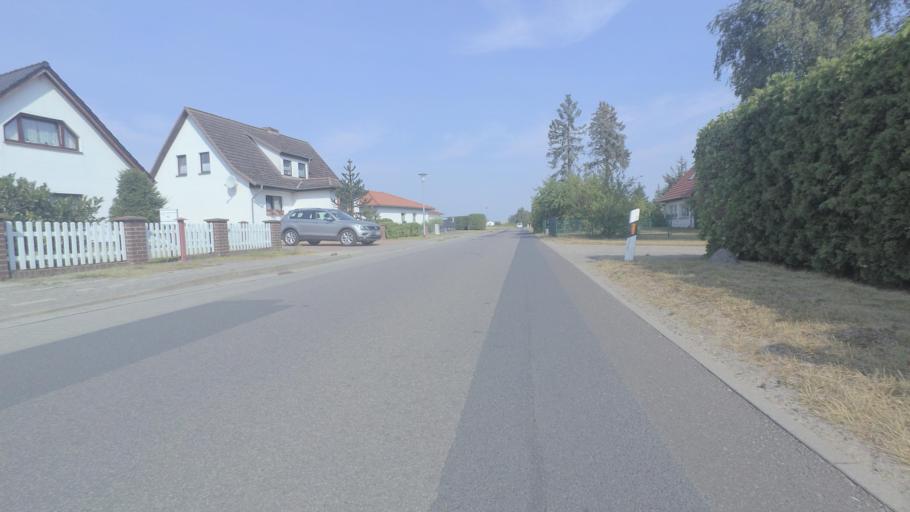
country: DE
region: Mecklenburg-Vorpommern
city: Wendorf
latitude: 54.2432
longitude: 13.0731
